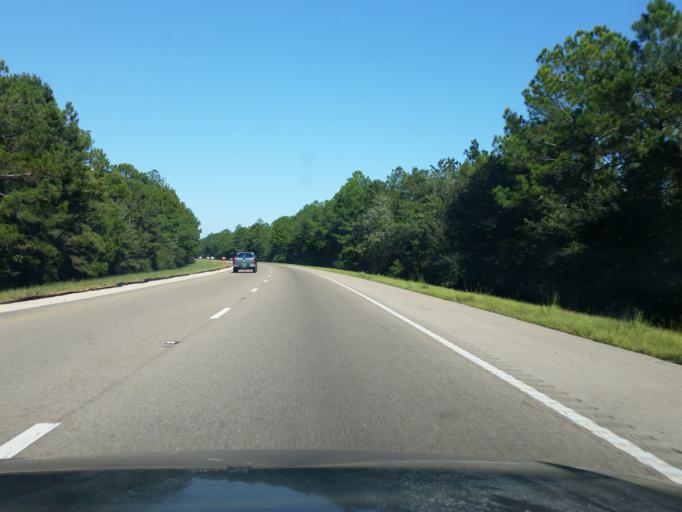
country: US
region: Mississippi
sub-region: Hancock County
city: Kiln
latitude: 30.3309
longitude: -89.5251
